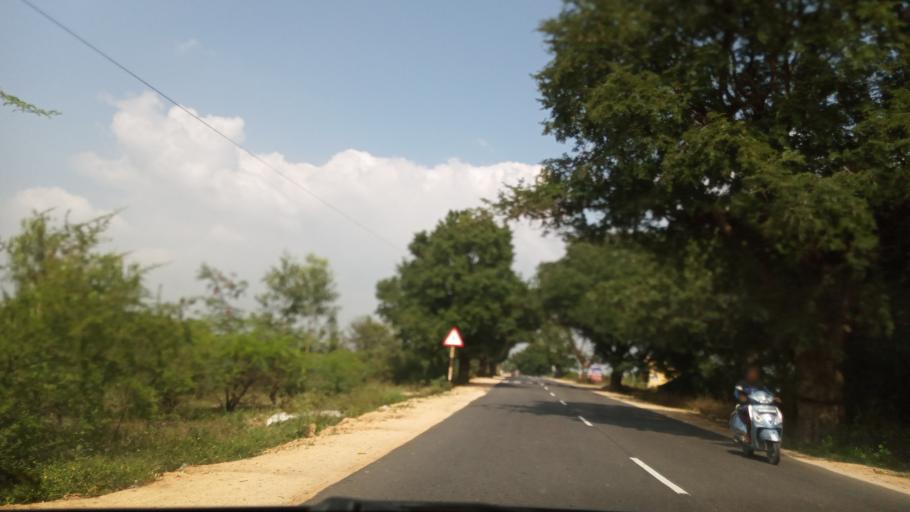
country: IN
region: Andhra Pradesh
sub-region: Chittoor
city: Madanapalle
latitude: 13.6063
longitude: 78.5371
